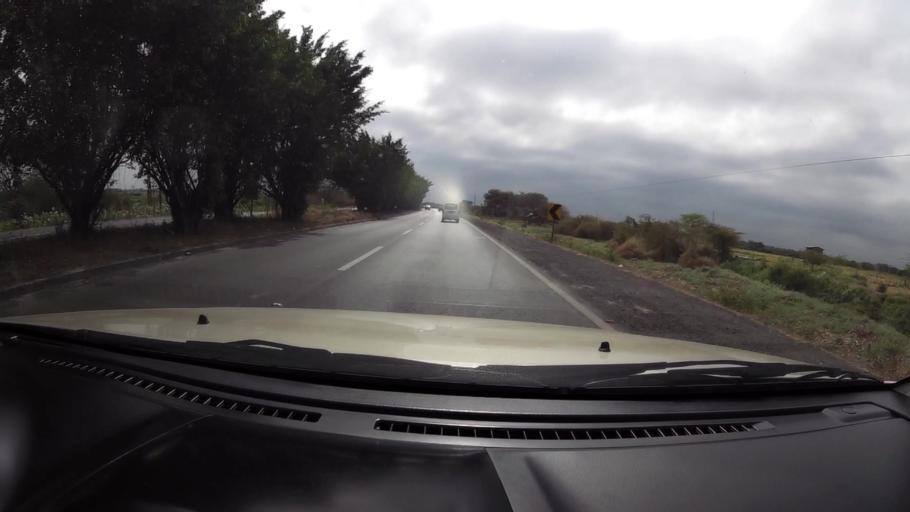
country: EC
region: Guayas
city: Yaguachi Nuevo
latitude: -2.2090
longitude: -79.7366
